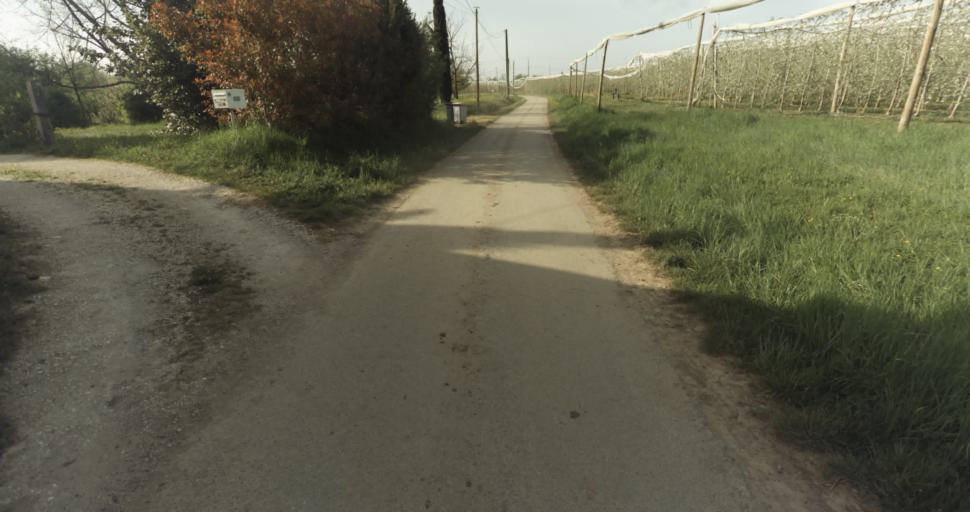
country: FR
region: Midi-Pyrenees
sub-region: Departement du Tarn-et-Garonne
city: Moissac
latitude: 44.1004
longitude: 1.1224
